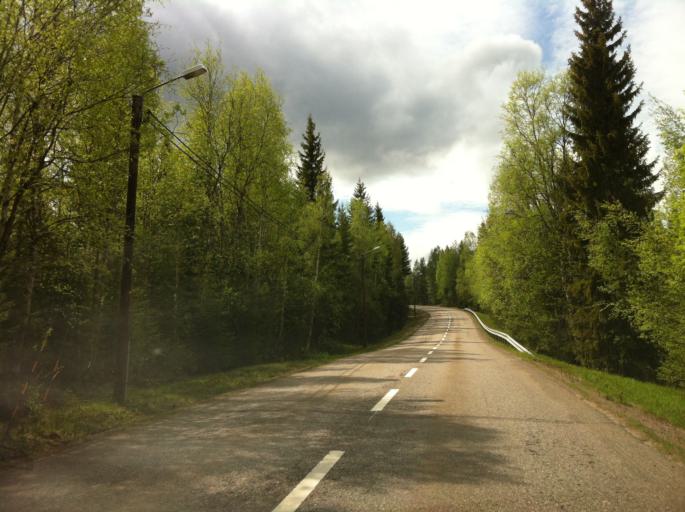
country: NO
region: Hedmark
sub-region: Trysil
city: Innbygda
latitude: 61.6888
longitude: 13.1372
